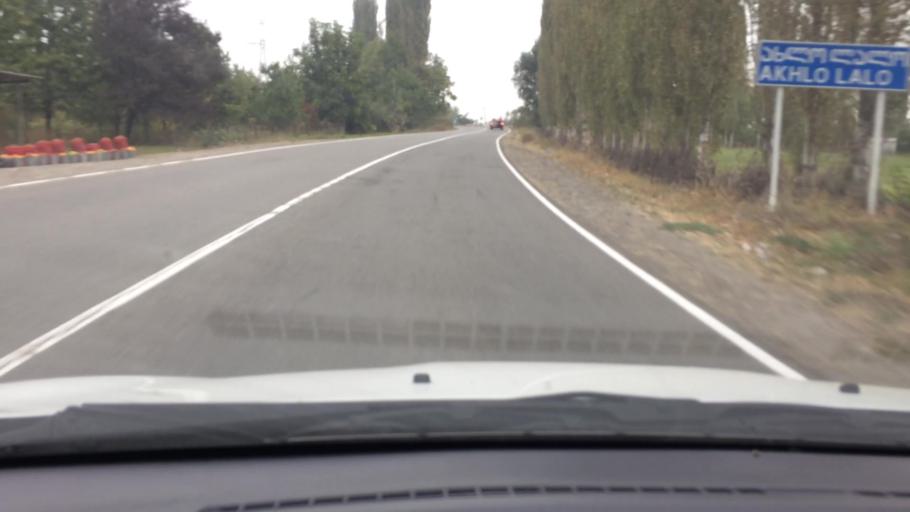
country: GE
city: Naghvarevi
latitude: 41.3048
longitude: 44.7902
